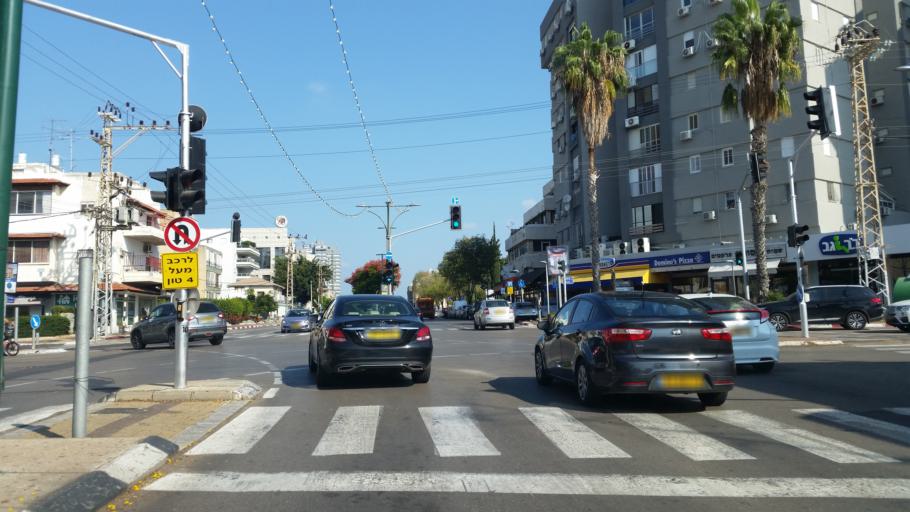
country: IL
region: Tel Aviv
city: Ramat HaSharon
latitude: 32.1607
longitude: 34.8425
